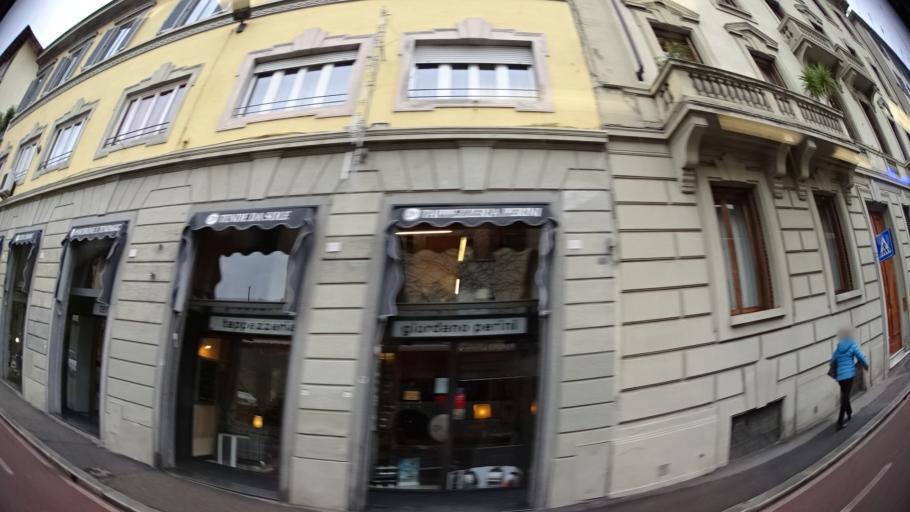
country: IT
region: Tuscany
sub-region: Province of Florence
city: Florence
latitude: 43.7835
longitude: 11.2636
